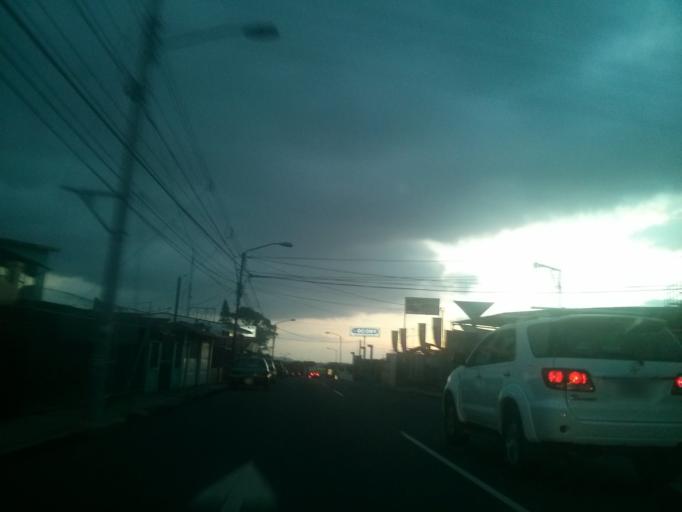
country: CR
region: San Jose
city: San Pedro
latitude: 9.9208
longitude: -84.0560
